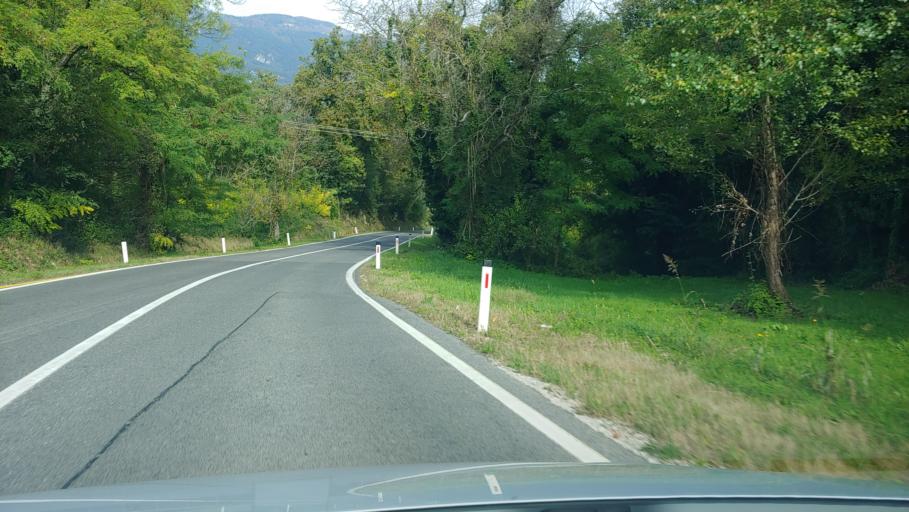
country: SI
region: Nova Gorica
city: Sempas
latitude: 45.8952
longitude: 13.7999
